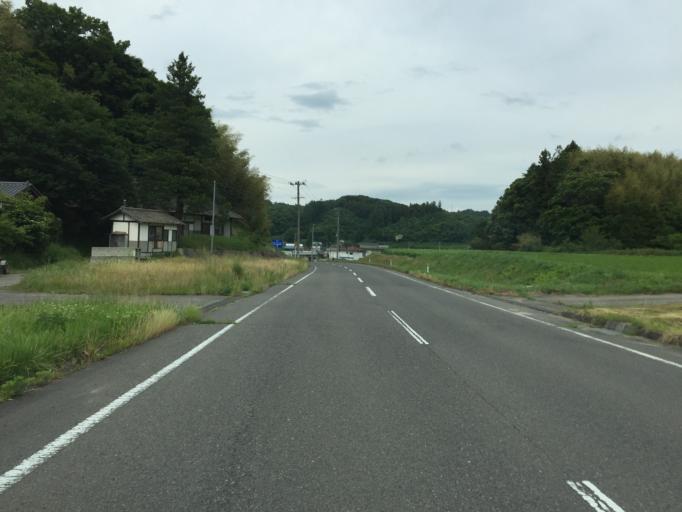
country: JP
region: Fukushima
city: Funehikimachi-funehiki
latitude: 37.4175
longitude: 140.6501
